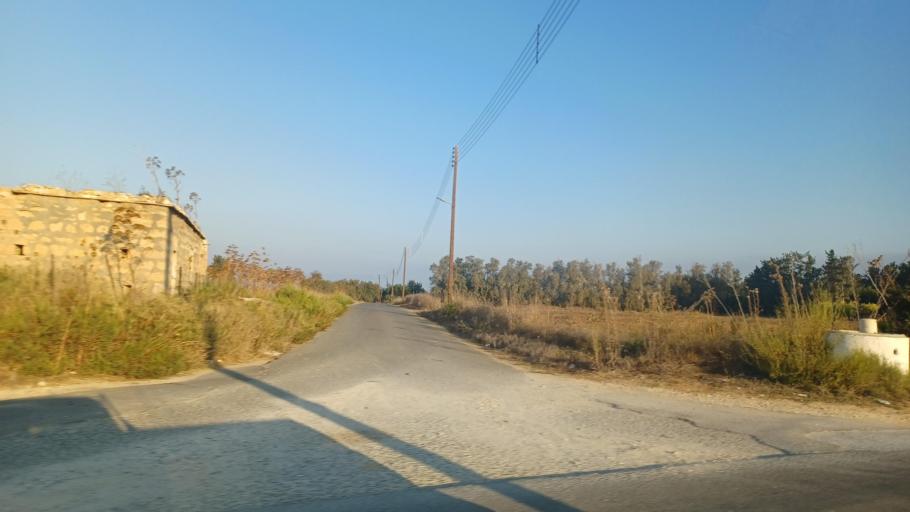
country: CY
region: Pafos
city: Empa
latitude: 34.8024
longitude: 32.4359
